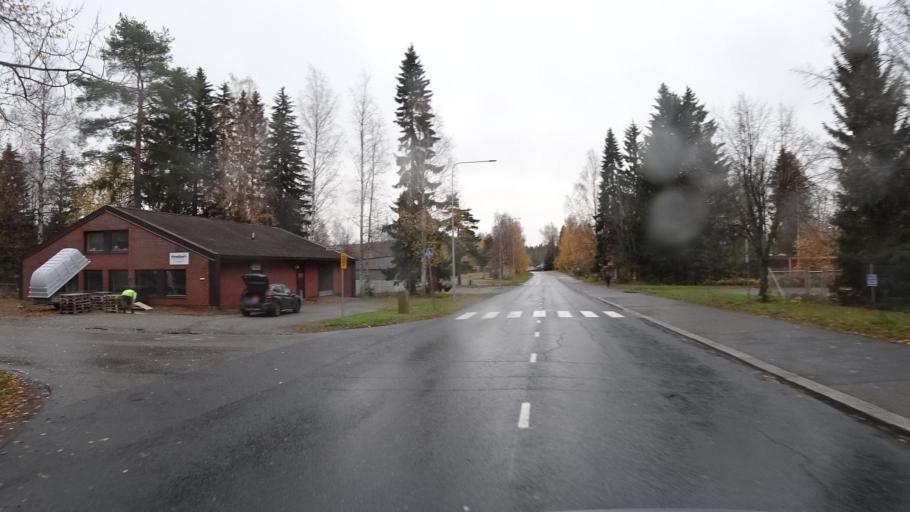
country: FI
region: Northern Savo
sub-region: Kuopio
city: Kuopio
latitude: 62.9279
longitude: 27.6891
